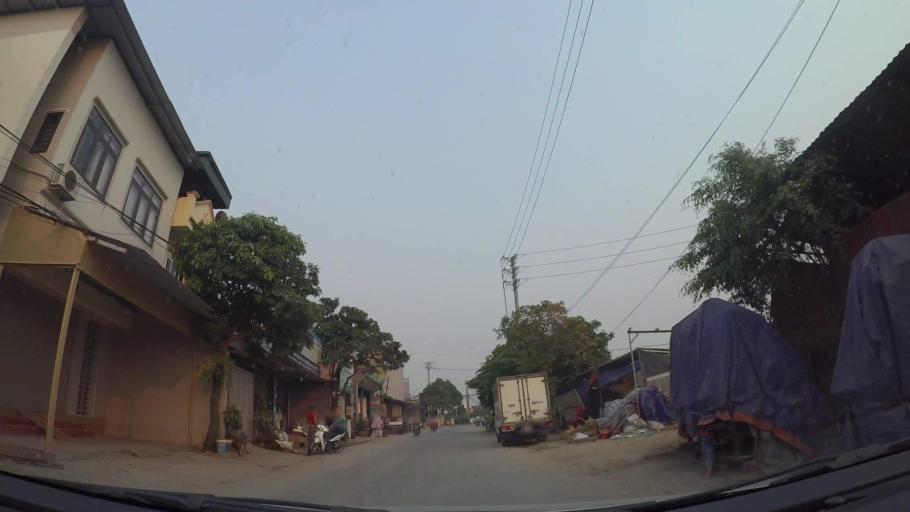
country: VN
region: Ha Noi
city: Cau Dien
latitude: 21.0039
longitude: 105.7221
